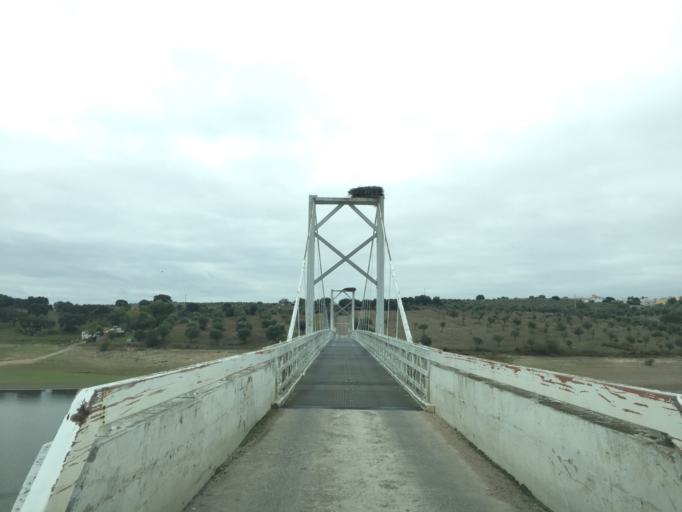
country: PT
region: Portalegre
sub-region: Avis
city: Avis
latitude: 39.0481
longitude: -7.8036
